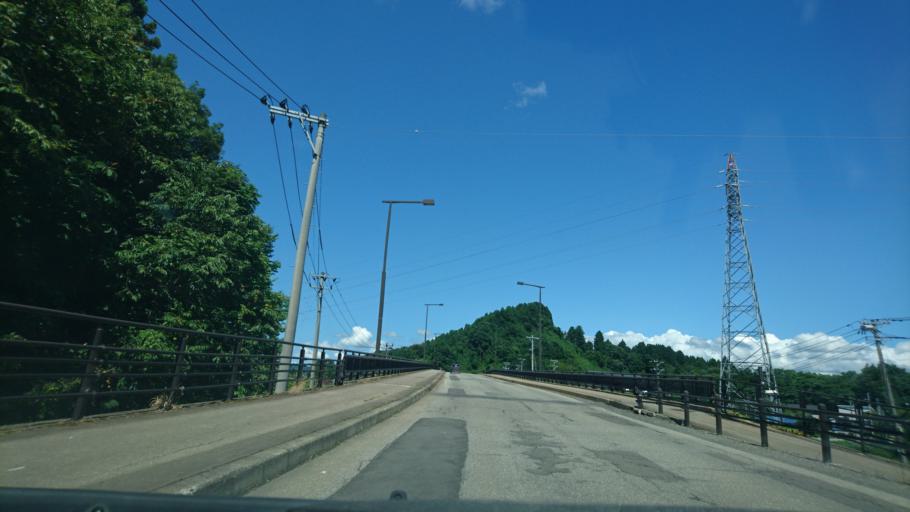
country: JP
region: Akita
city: Kakunodatemachi
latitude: 39.5872
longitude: 140.5703
